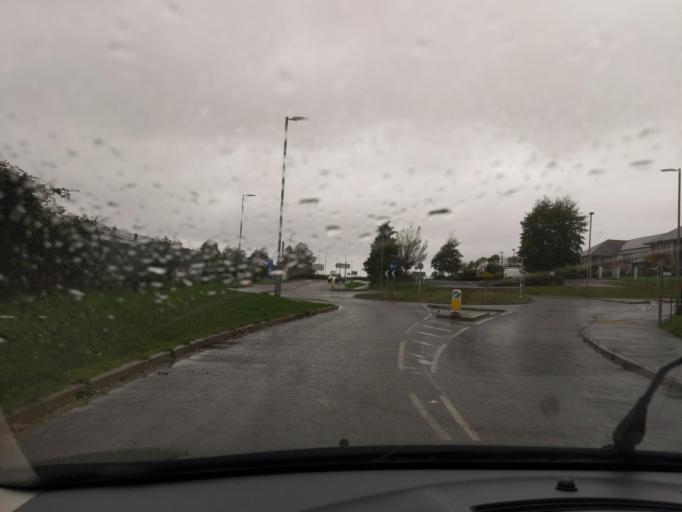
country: GB
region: England
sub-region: Cornwall
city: Wadebridge
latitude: 50.5210
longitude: -4.8229
